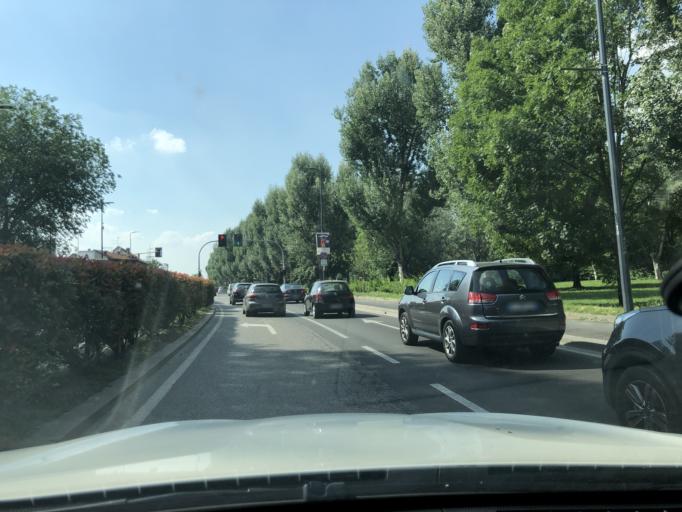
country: IT
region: Lombardy
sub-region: Citta metropolitana di Milano
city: Novate Milanese
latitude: 45.5180
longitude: 9.1554
